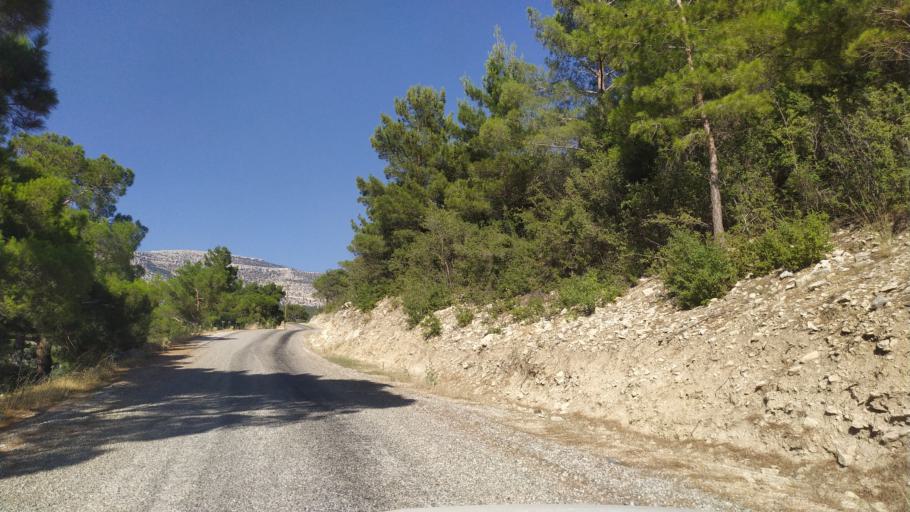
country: TR
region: Mersin
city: Mut
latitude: 36.7026
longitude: 33.4725
